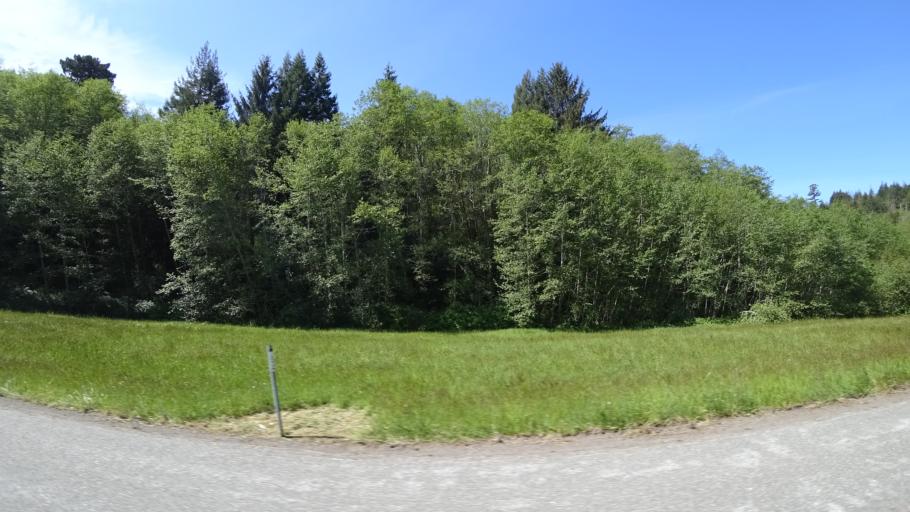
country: US
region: California
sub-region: Del Norte County
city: Bertsch-Oceanview
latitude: 41.4601
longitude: -124.0335
